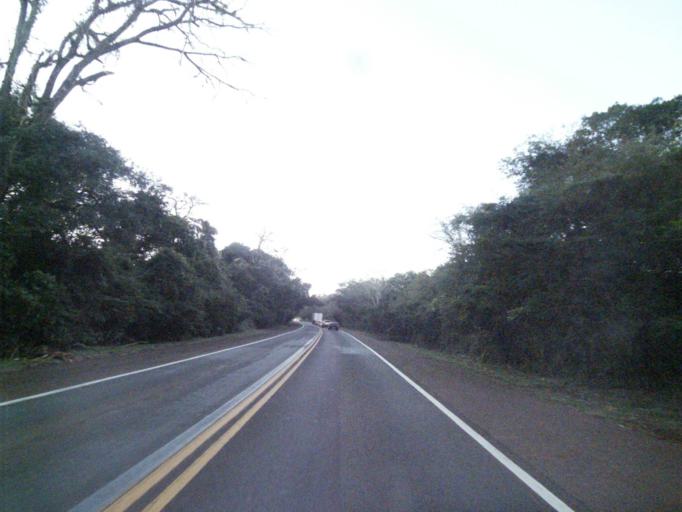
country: BR
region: Parana
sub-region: Londrina
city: Londrina
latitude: -23.4497
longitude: -51.1317
